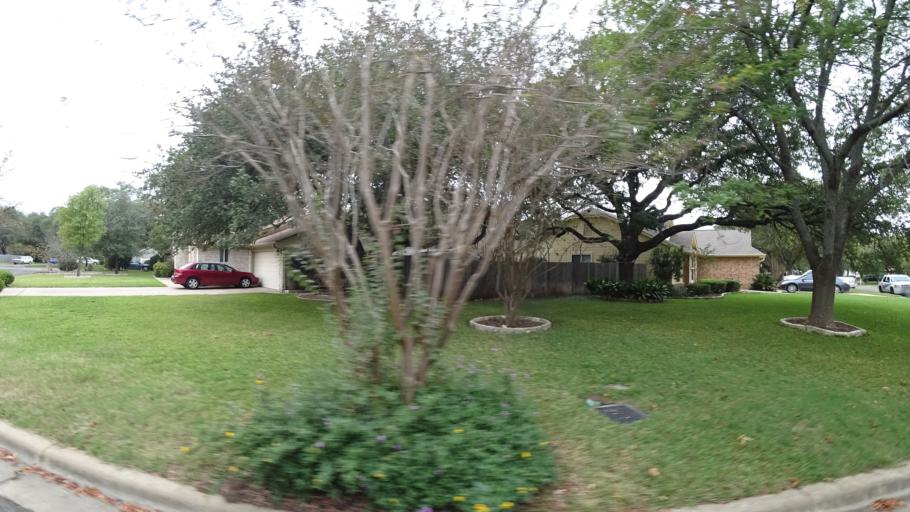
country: US
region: Texas
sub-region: Williamson County
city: Round Rock
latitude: 30.4849
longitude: -97.7012
